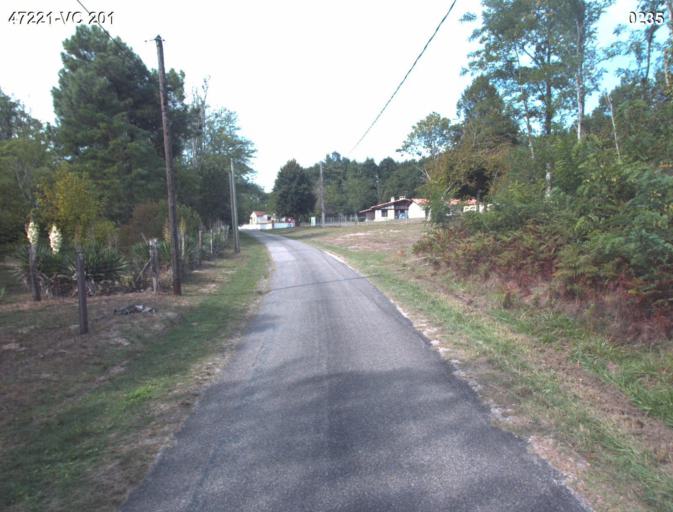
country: FR
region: Aquitaine
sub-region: Departement du Lot-et-Garonne
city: Mezin
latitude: 44.1180
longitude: 0.2261
